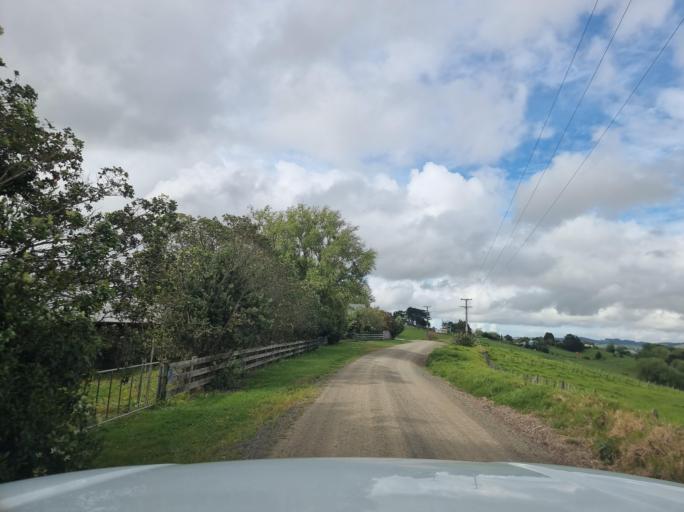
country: NZ
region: Northland
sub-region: Whangarei
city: Ruakaka
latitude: -36.1273
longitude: 174.2082
